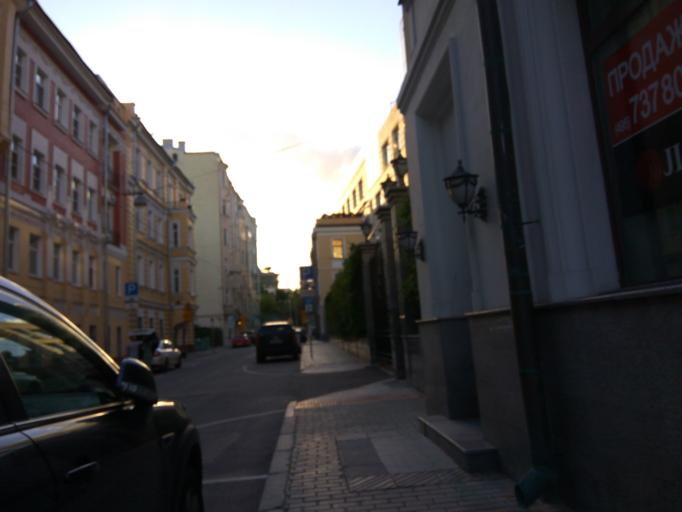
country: RU
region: Moscow
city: Moscow
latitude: 55.7401
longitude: 37.5932
